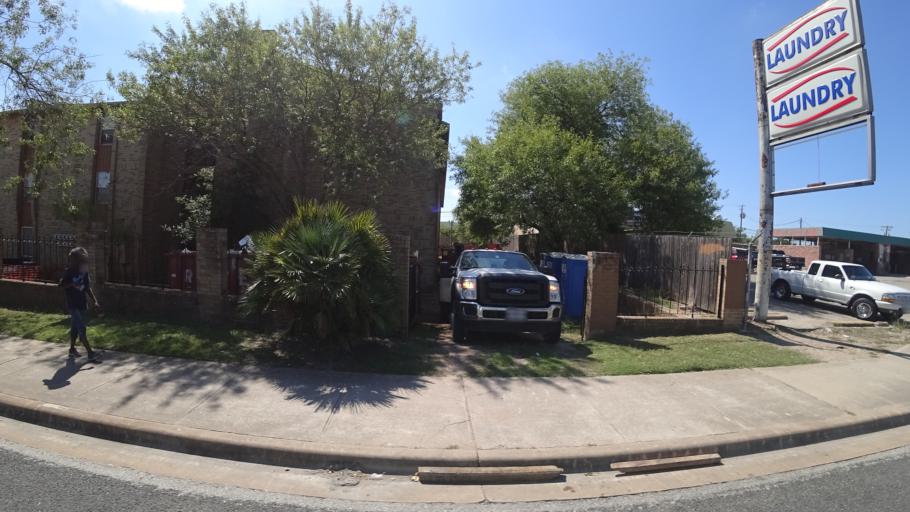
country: US
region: Texas
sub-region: Travis County
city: Austin
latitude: 30.3129
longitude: -97.6894
